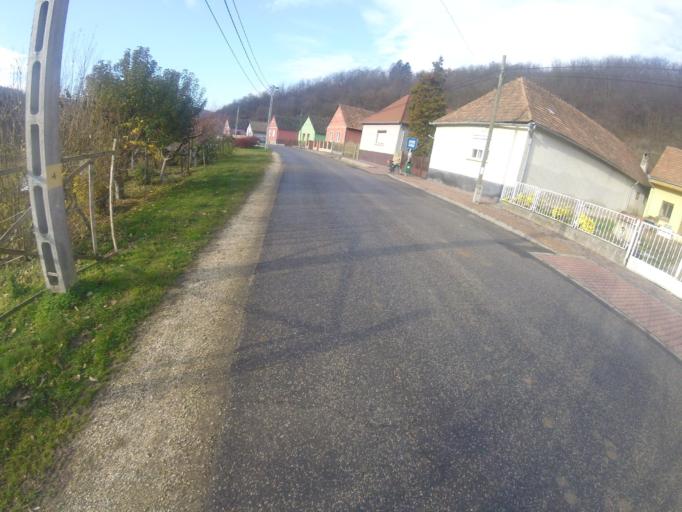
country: HU
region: Tolna
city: Bonyhad
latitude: 46.2249
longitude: 18.6057
